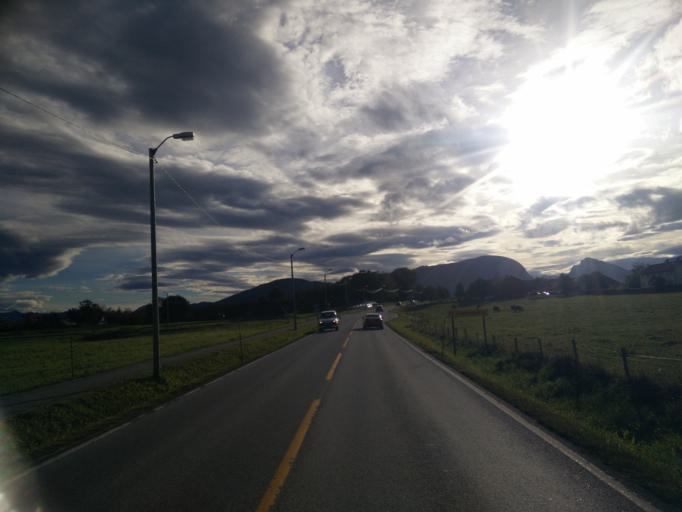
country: NO
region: More og Romsdal
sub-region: Vestnes
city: Vestnes
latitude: 62.6308
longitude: 7.0733
